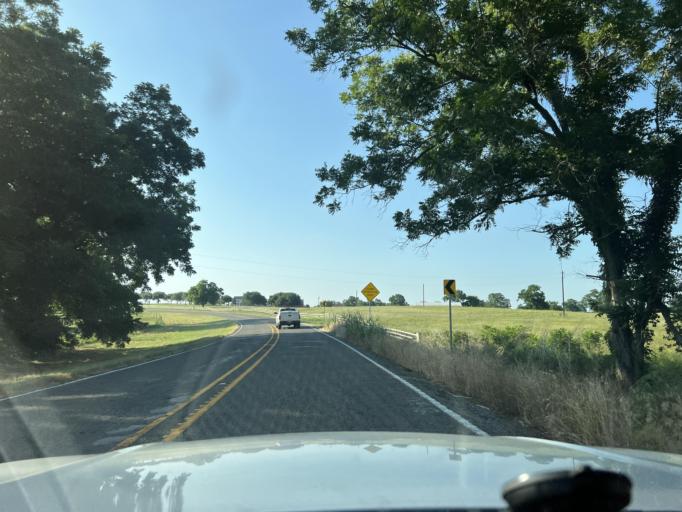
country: US
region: Texas
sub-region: Washington County
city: Brenham
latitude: 30.2354
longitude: -96.2392
